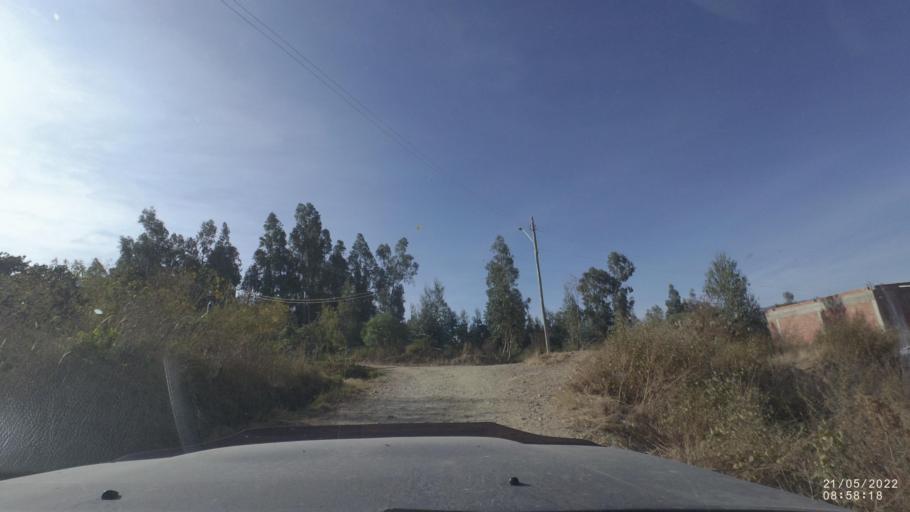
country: BO
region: Cochabamba
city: Cochabamba
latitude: -17.3800
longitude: -66.0383
